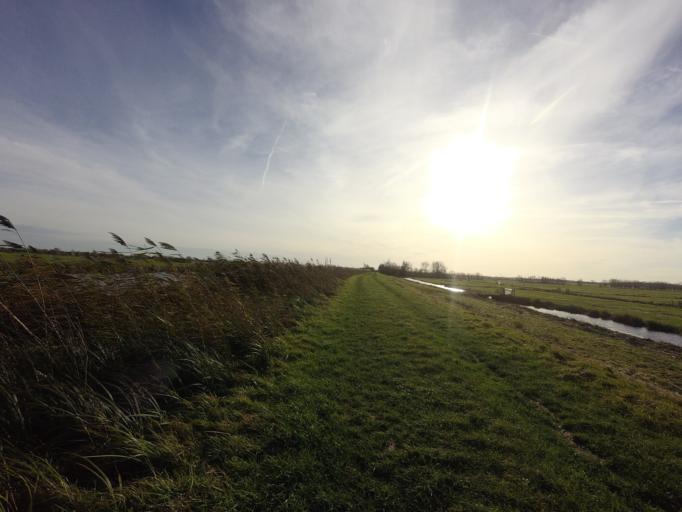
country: NL
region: South Holland
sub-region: Gemeente Vlist
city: Haastrecht
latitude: 52.0439
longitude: 4.7804
